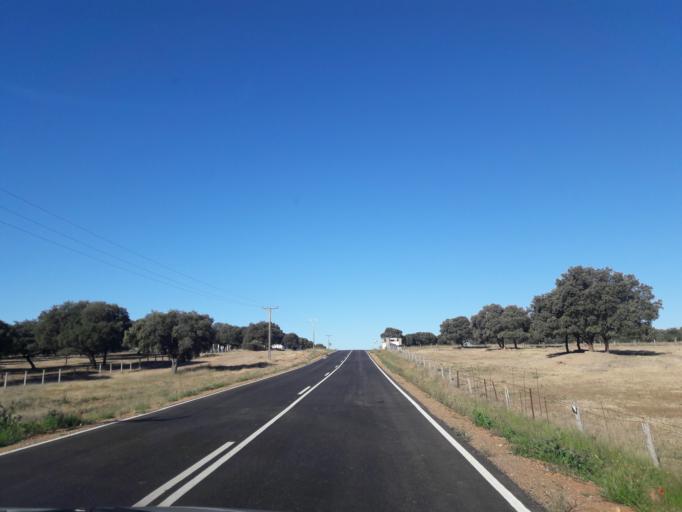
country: ES
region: Castille and Leon
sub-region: Provincia de Salamanca
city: Calzada de Don Diego
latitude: 40.8553
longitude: -5.8636
